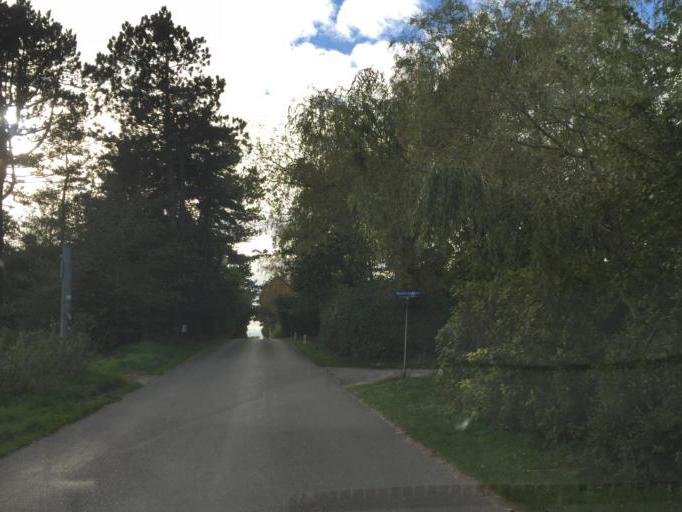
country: DK
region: Zealand
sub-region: Odsherred Kommune
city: Asnaes
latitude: 55.8390
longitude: 11.4559
